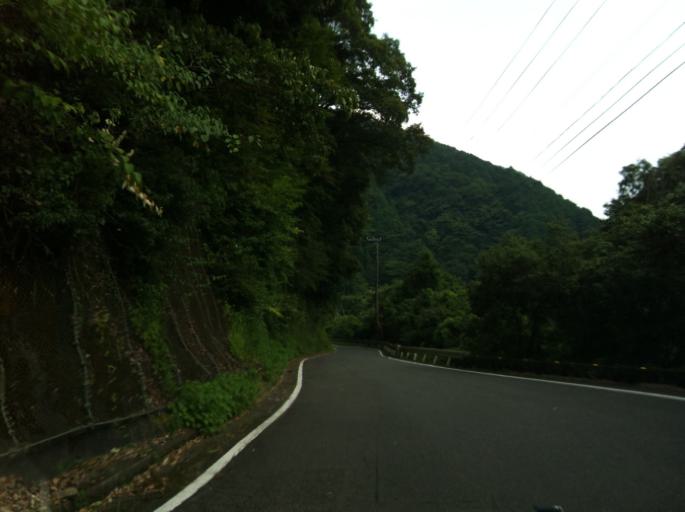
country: JP
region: Shizuoka
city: Shizuoka-shi
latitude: 35.2043
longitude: 138.3567
